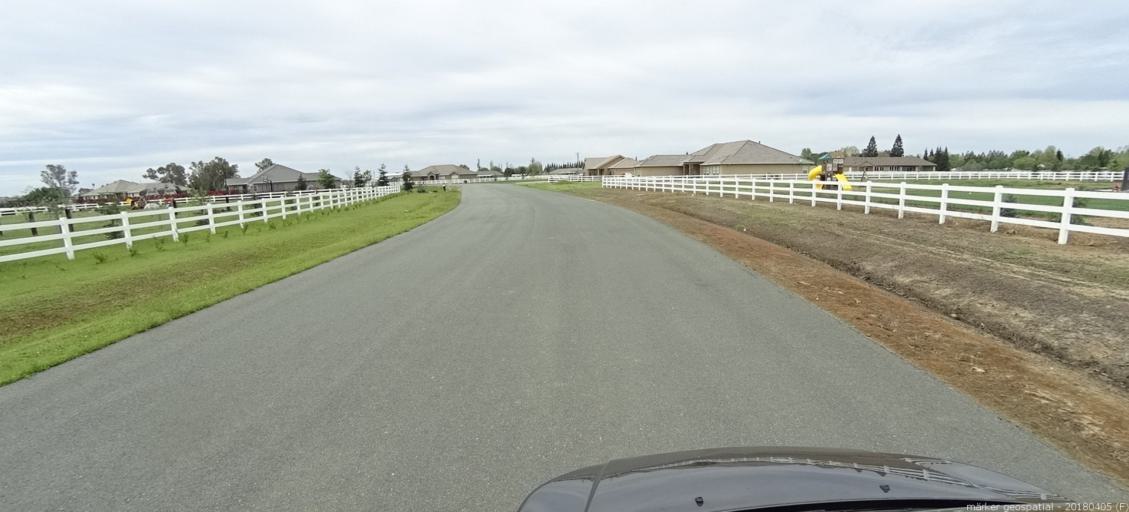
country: US
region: California
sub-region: Sacramento County
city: Galt
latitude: 38.2861
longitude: -121.3213
